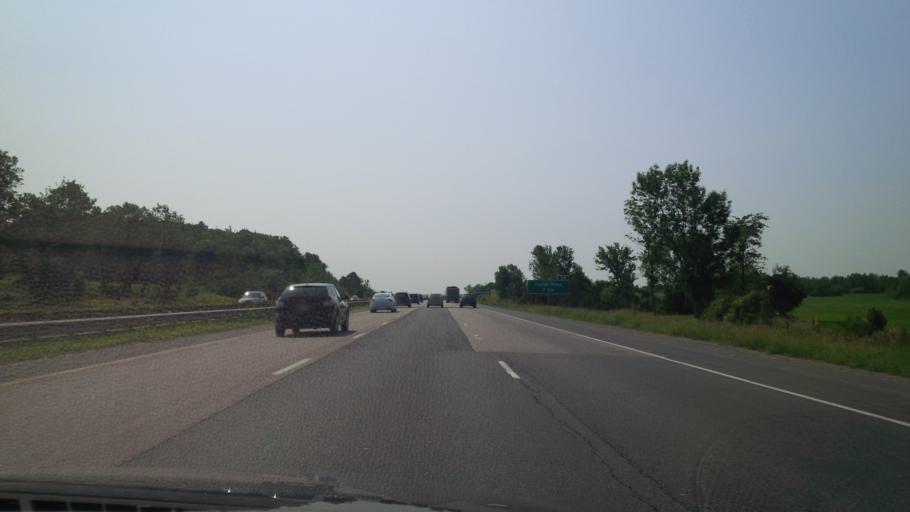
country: CA
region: Ontario
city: Bradford West Gwillimbury
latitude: 44.0600
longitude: -79.6162
